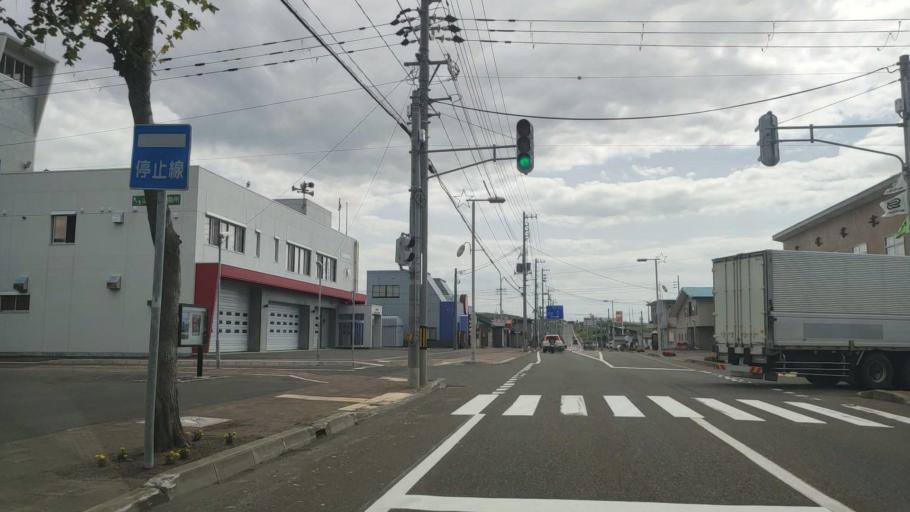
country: JP
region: Hokkaido
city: Rumoi
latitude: 44.5330
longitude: 141.7669
